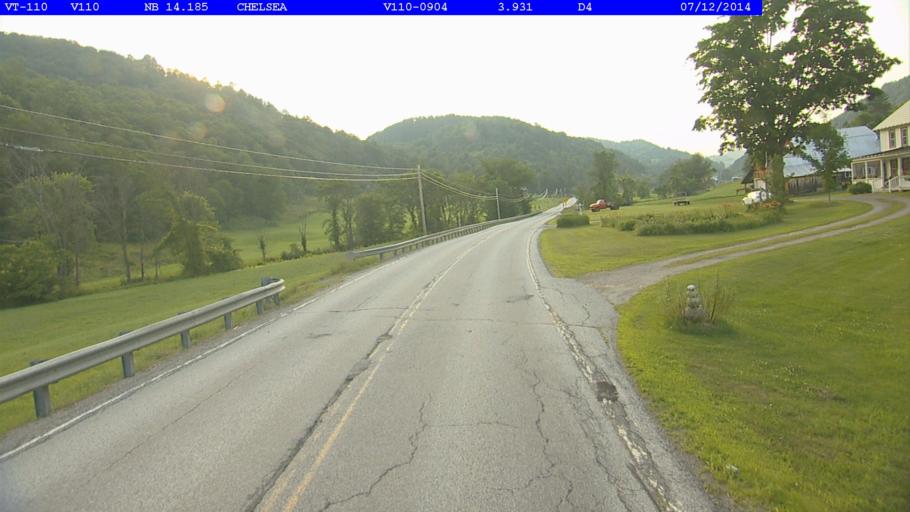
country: US
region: Vermont
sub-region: Orange County
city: Chelsea
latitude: 44.0008
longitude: -72.4540
